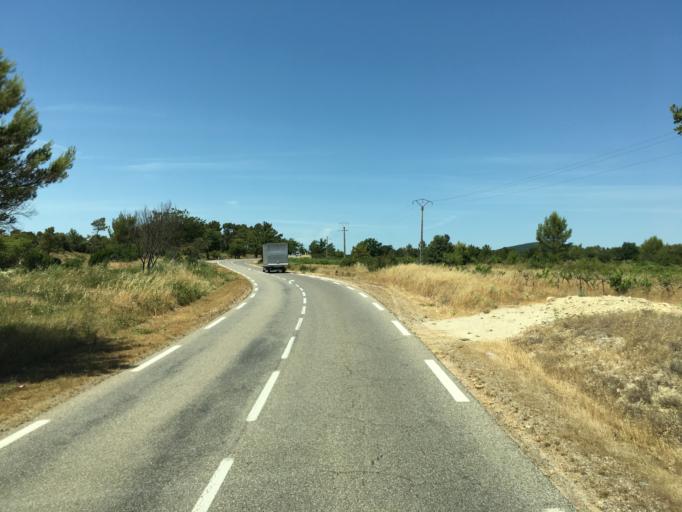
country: FR
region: Provence-Alpes-Cote d'Azur
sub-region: Departement du Var
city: Saint-Maximin-la-Sainte-Baume
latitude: 43.4905
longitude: 5.8171
